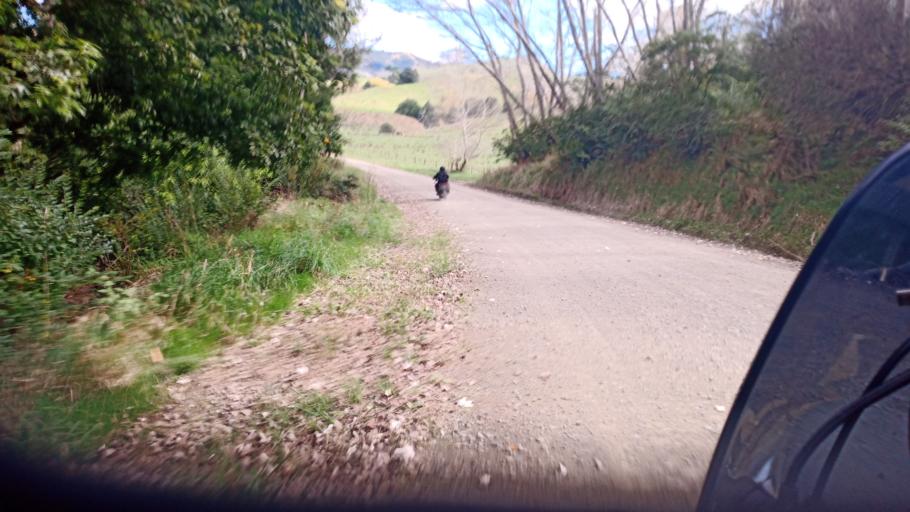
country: NZ
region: Gisborne
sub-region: Gisborne District
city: Gisborne
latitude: -38.4236
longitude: 177.7216
